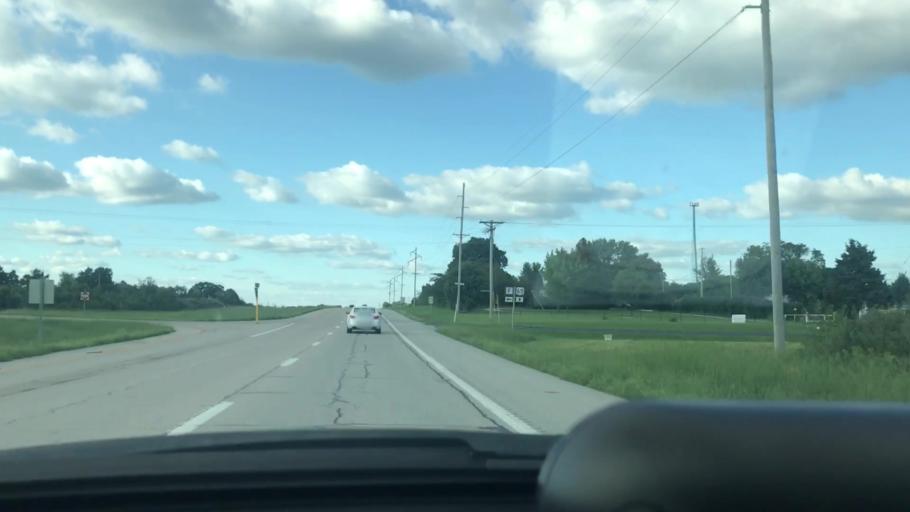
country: US
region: Missouri
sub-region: Pettis County
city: Sedalia
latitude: 38.6256
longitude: -93.2673
